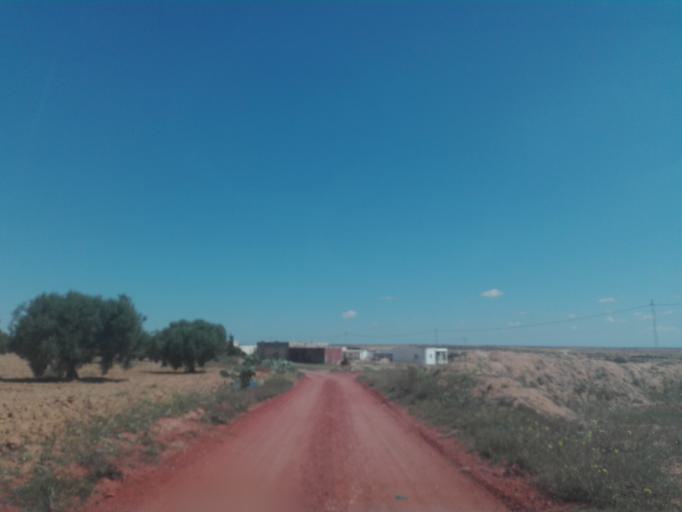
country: TN
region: Safaqis
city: Sfax
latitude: 34.7326
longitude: 10.4332
